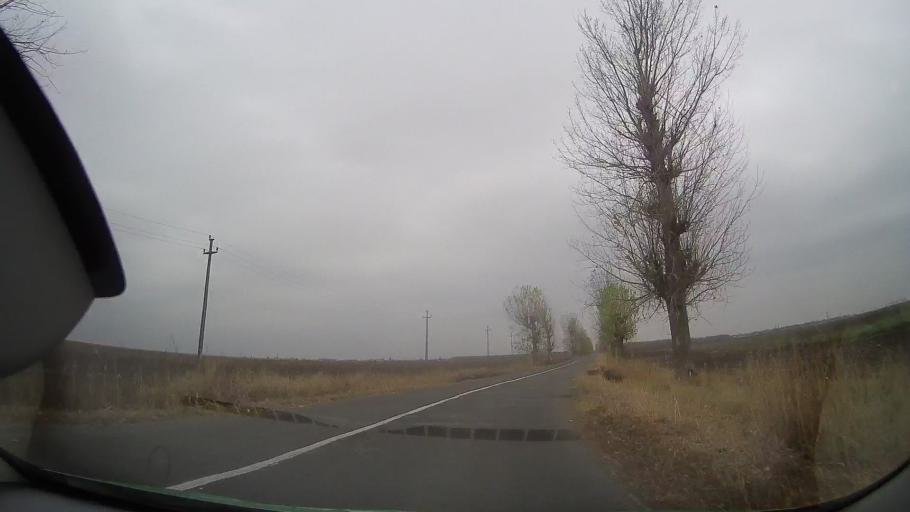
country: RO
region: Ialomita
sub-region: Comuna Grindu
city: Grindu
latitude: 44.7916
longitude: 26.9000
